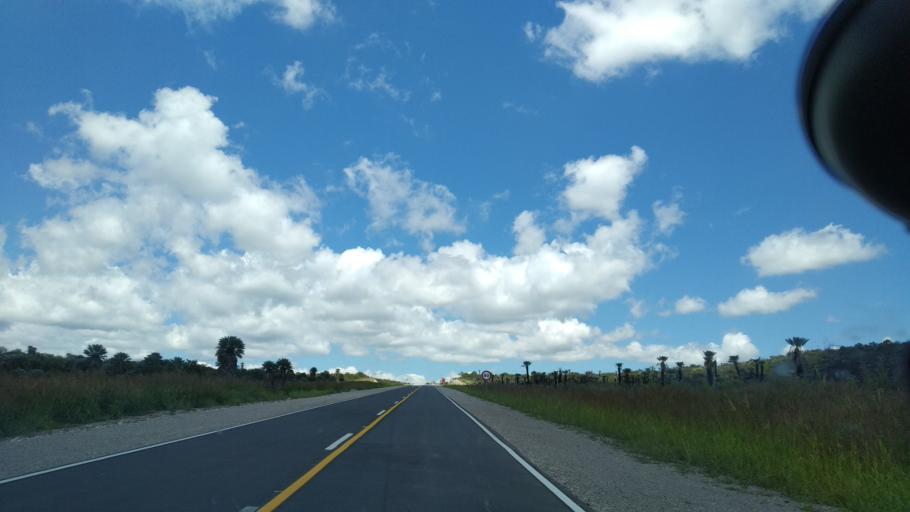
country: AR
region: Cordoba
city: Salsacate
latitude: -31.3733
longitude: -65.2706
